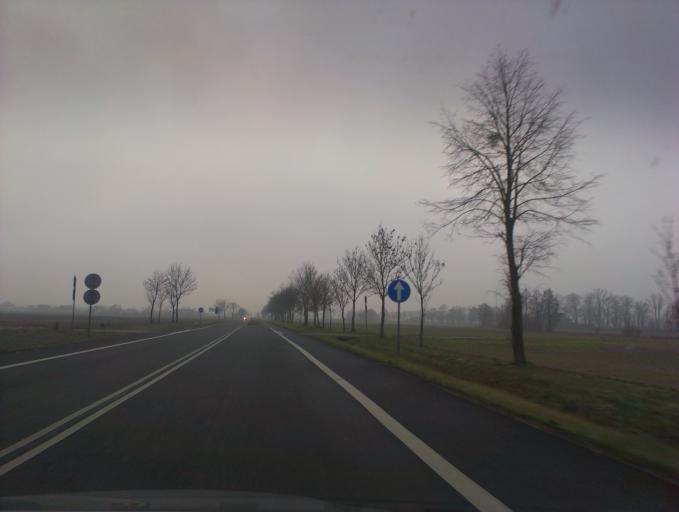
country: PL
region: Greater Poland Voivodeship
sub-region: Powiat chodzieski
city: Budzyn
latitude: 52.8981
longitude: 16.9698
